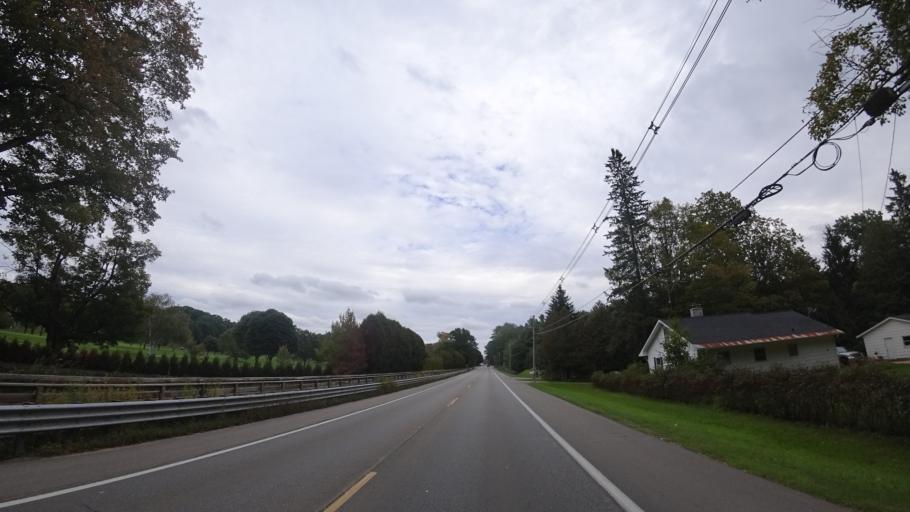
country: US
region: Michigan
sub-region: Emmet County
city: Harbor Springs
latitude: 45.4315
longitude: -84.9613
